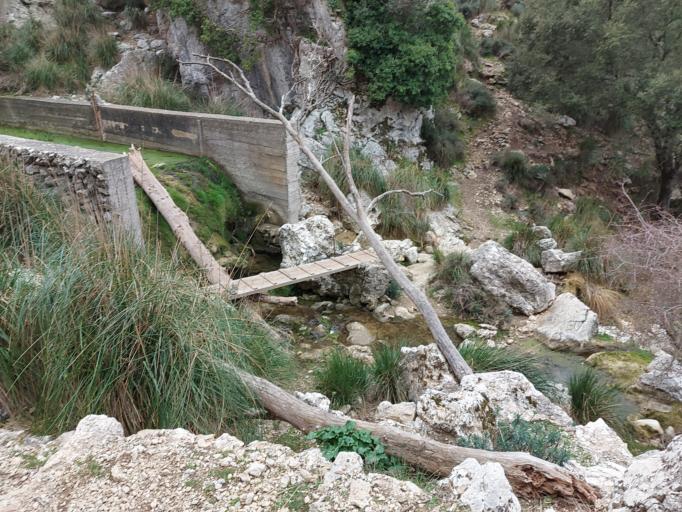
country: ES
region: Balearic Islands
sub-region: Illes Balears
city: Fornalutx
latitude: 39.7594
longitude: 2.7561
